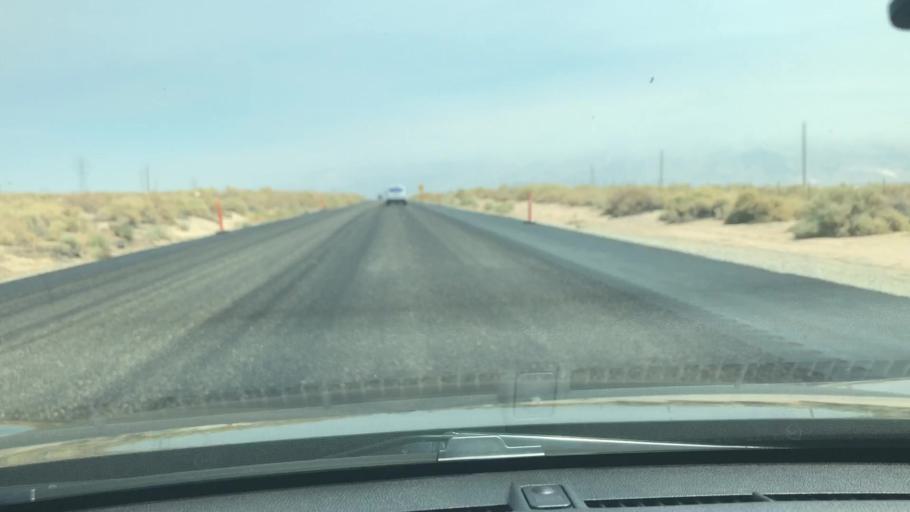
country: US
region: California
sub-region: Inyo County
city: Lone Pine
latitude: 36.4878
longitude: -118.0341
